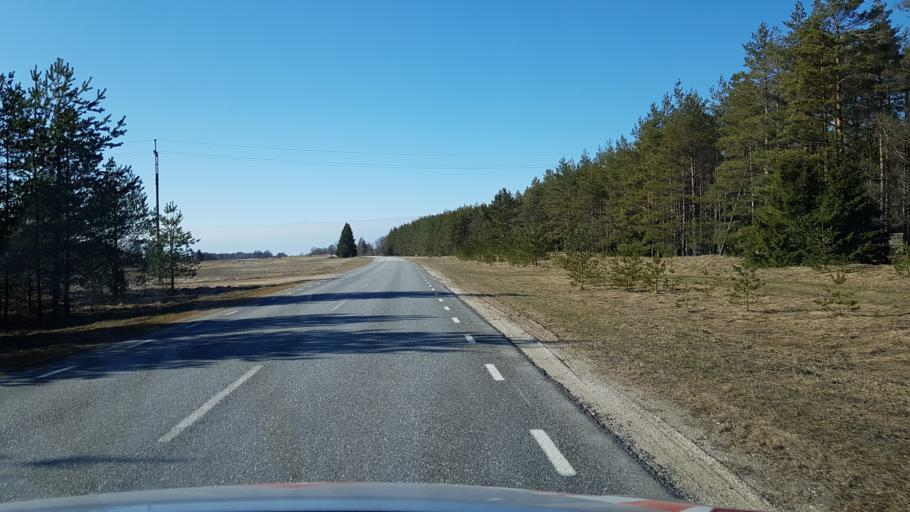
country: EE
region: Laeaene-Virumaa
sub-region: Haljala vald
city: Haljala
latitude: 59.4666
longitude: 26.1818
